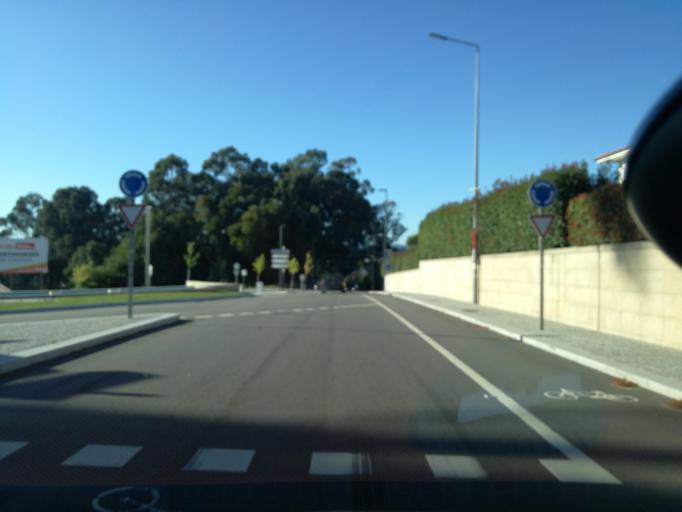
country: PT
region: Porto
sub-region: Santo Tirso
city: Santo Tirso
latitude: 41.3347
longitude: -8.4791
